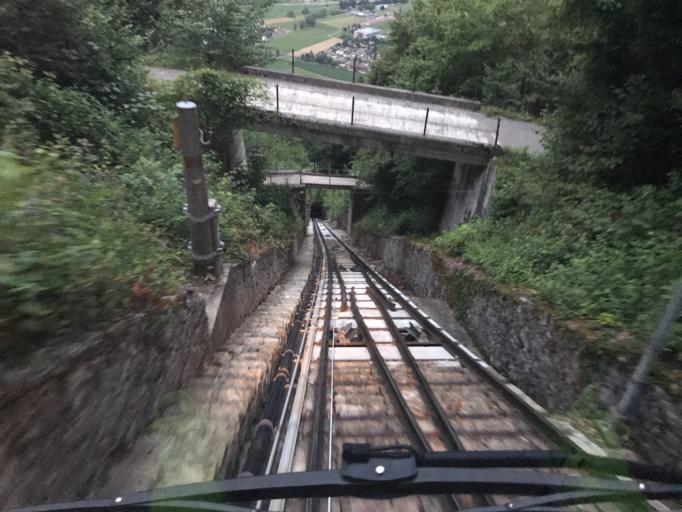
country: CH
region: Bern
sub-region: Interlaken-Oberhasli District
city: Interlaken
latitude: 46.6957
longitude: 7.8625
